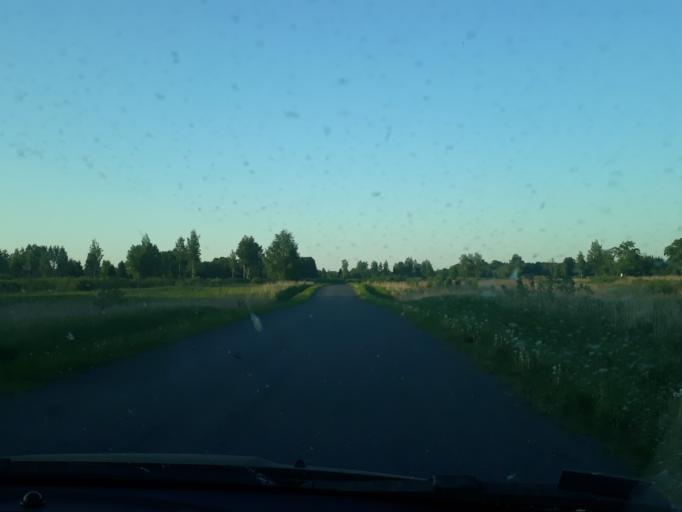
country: EE
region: Paernumaa
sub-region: Vaendra vald (alev)
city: Vandra
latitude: 58.5671
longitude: 24.9816
